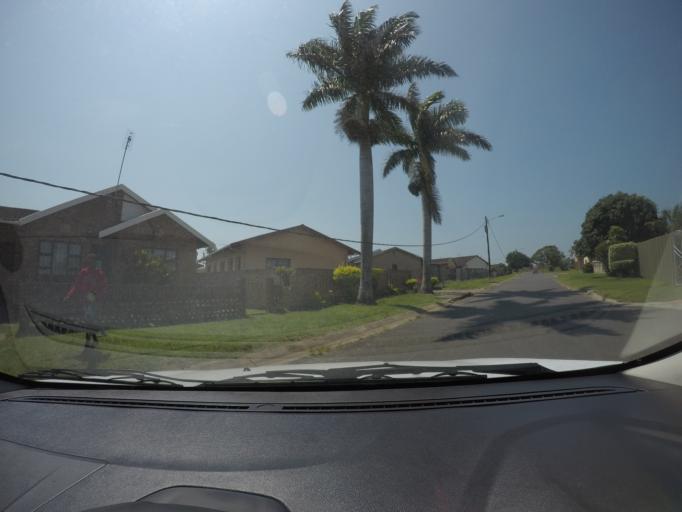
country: ZA
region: KwaZulu-Natal
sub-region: uThungulu District Municipality
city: eSikhawini
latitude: -28.8633
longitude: 31.9232
